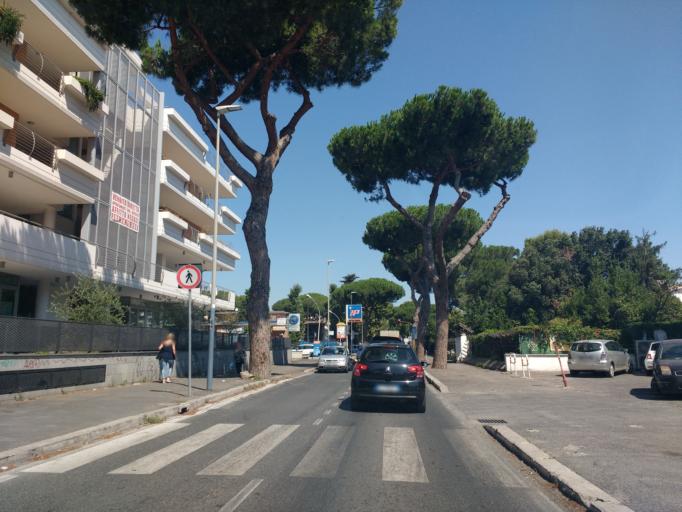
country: IT
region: Latium
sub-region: Citta metropolitana di Roma Capitale
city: Acilia-Castel Fusano-Ostia Antica
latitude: 41.7807
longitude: 12.3668
